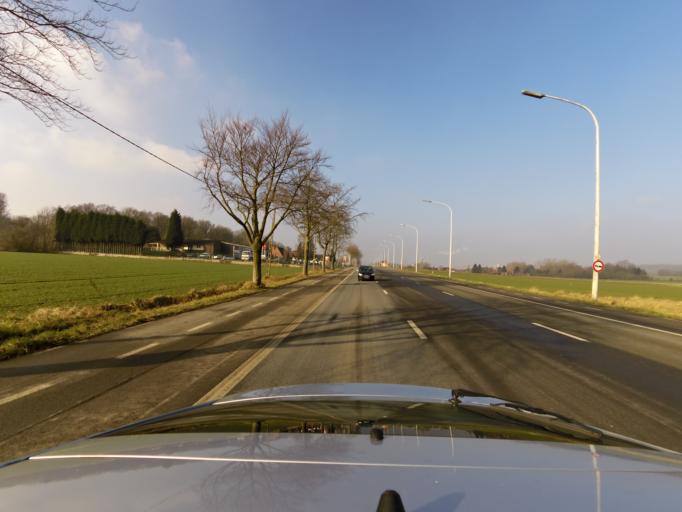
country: BE
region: Wallonia
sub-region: Province du Hainaut
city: Antoing
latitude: 50.5950
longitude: 3.5174
